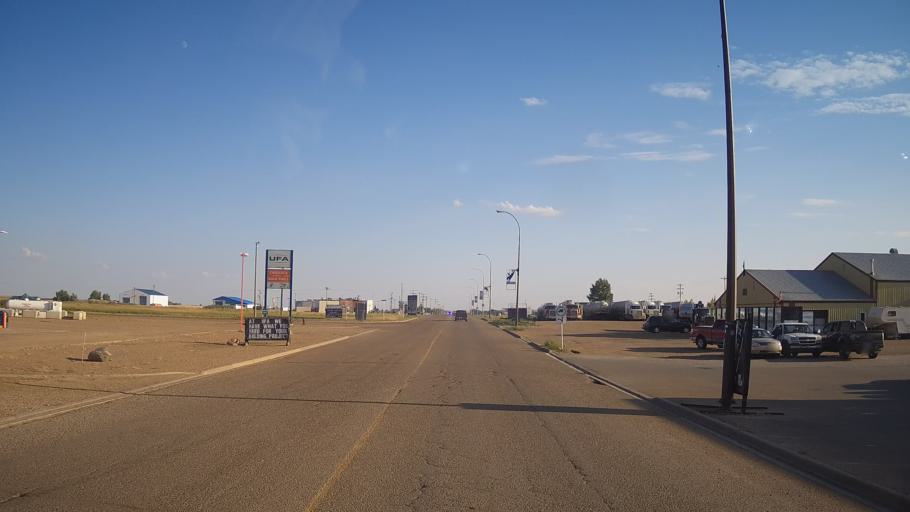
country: CA
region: Alberta
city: Hanna
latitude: 51.6396
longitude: -111.9423
